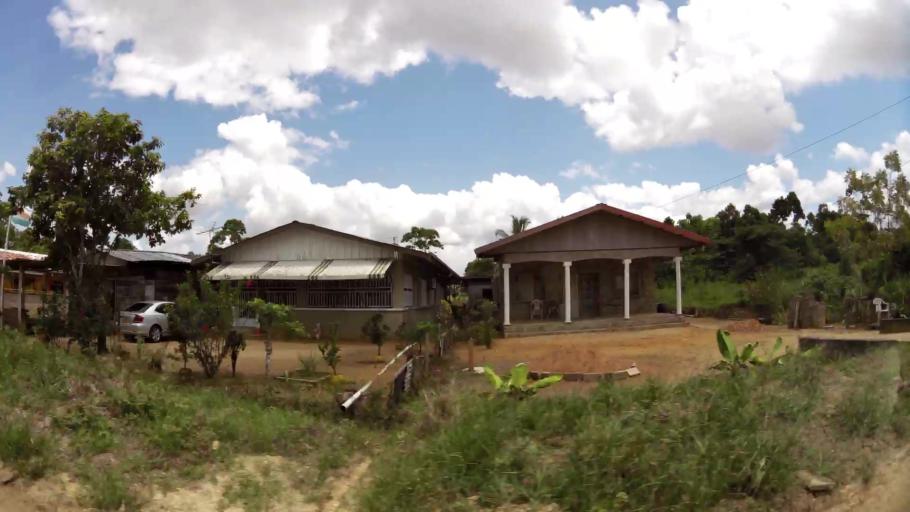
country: SR
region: Paramaribo
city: Paramaribo
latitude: 5.7997
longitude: -55.1376
